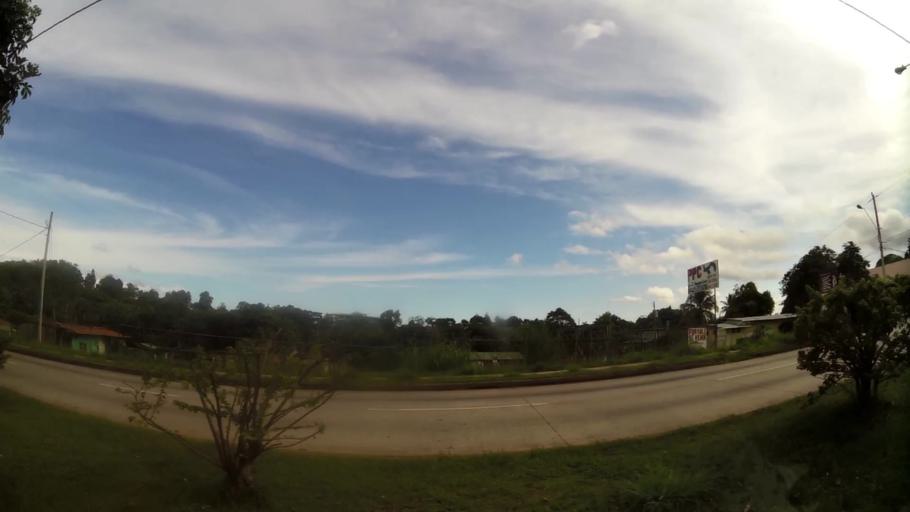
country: PA
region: Panama
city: Guadalupe
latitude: 8.8627
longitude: -79.8061
